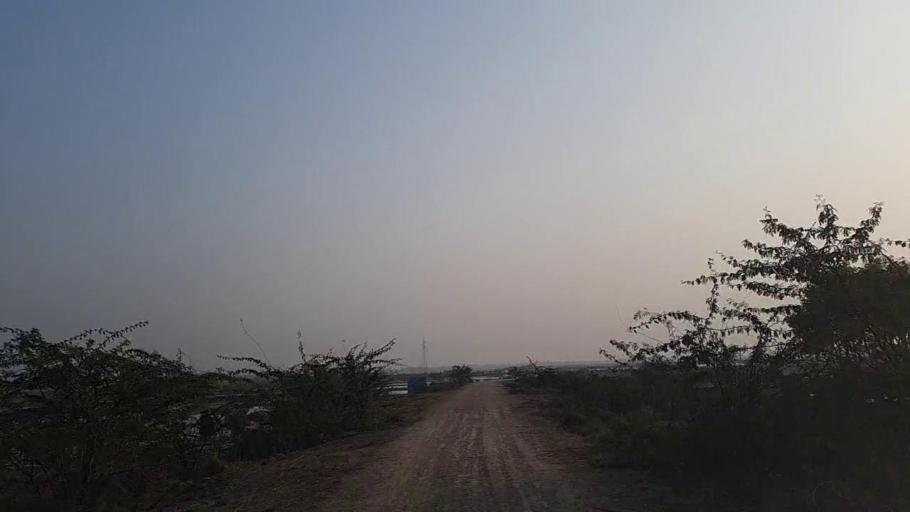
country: PK
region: Sindh
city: Nawabshah
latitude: 26.2367
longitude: 68.4710
